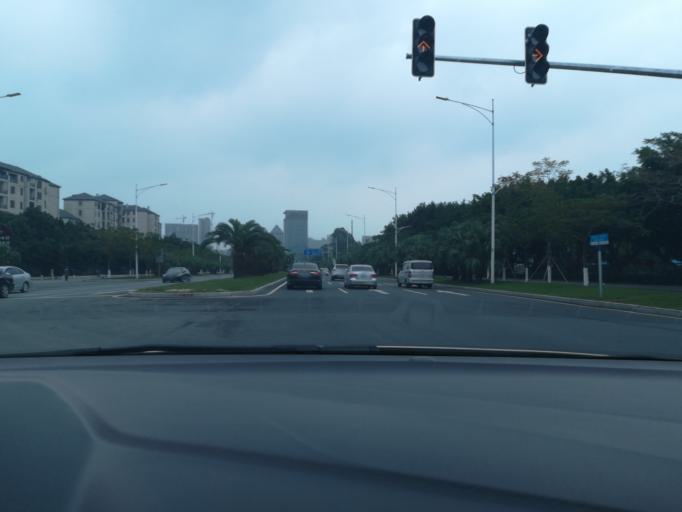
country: CN
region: Guangdong
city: Nansha
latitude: 22.7795
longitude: 113.5952
